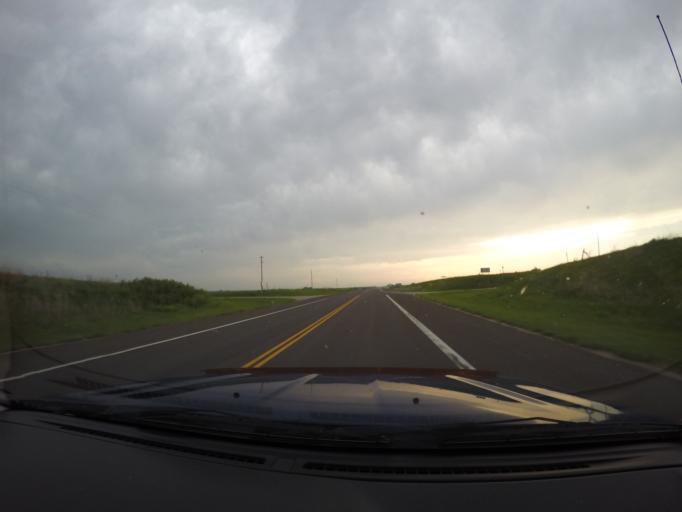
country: US
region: Kansas
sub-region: Clay County
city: Clay Center
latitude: 39.3796
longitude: -96.9792
